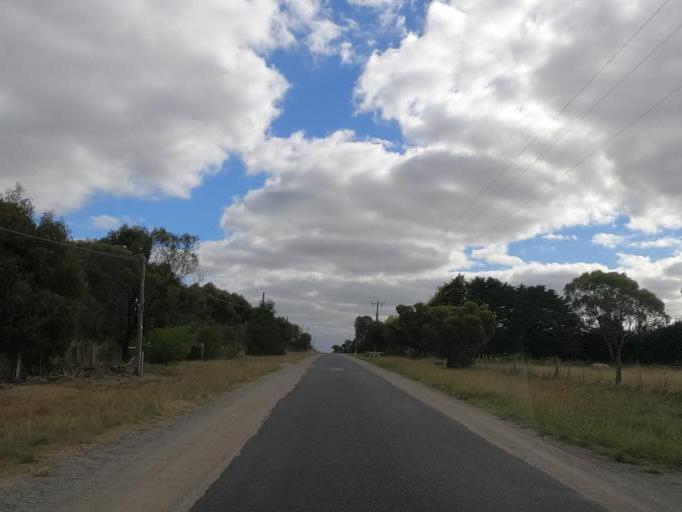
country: AU
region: Victoria
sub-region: Hume
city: Greenvale
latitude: -37.5619
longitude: 144.8735
